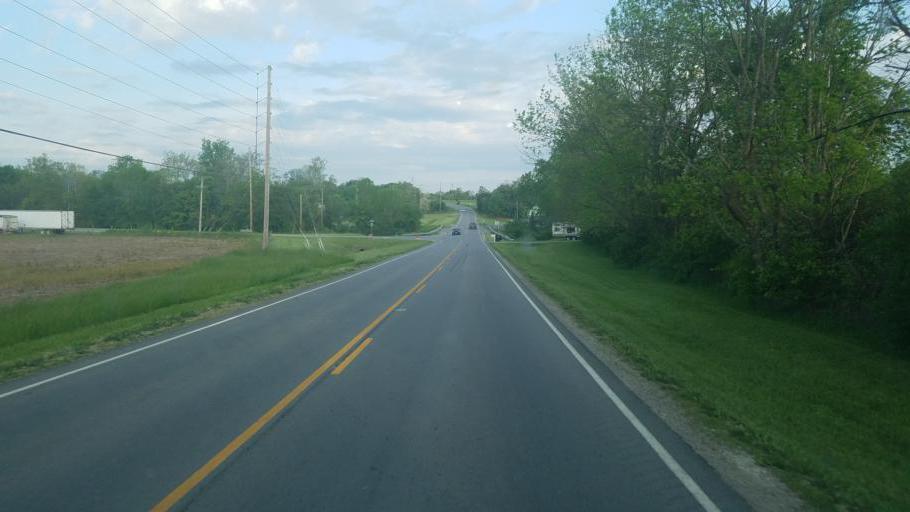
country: US
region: Ohio
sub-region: Highland County
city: Leesburg
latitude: 39.3471
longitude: -83.5821
